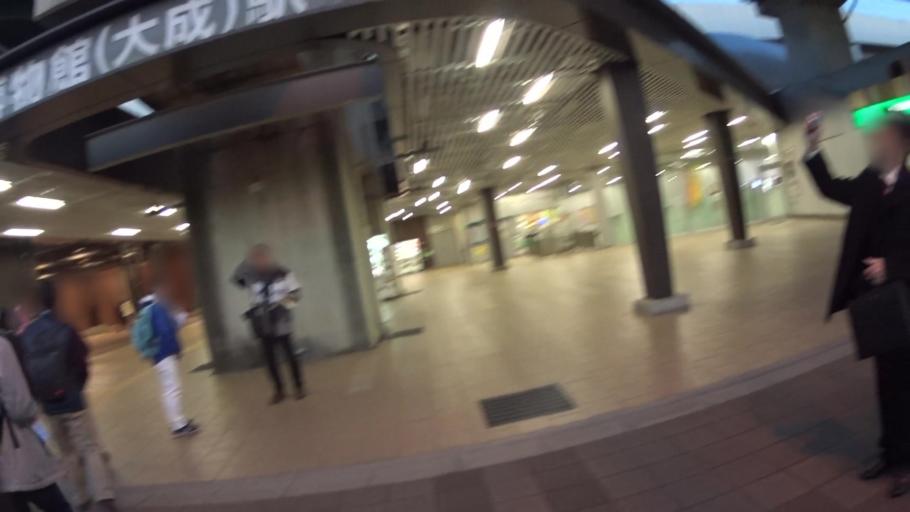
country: JP
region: Saitama
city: Yono
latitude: 35.9203
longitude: 139.6161
